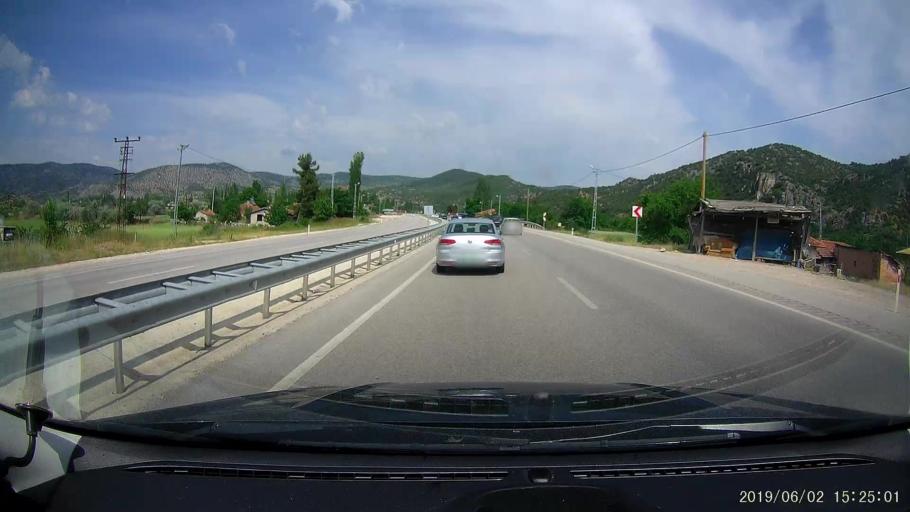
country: TR
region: Amasya
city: Saraycik
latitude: 40.9924
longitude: 35.0130
